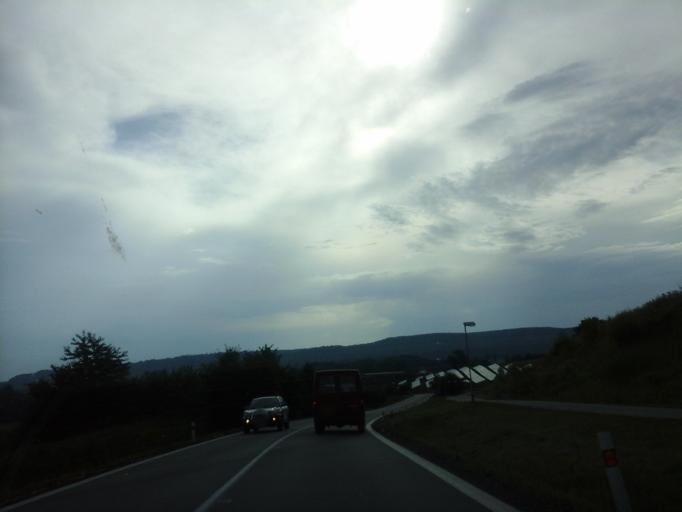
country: CZ
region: Pardubicky
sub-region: Okres Usti nad Orlici
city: Lanskroun
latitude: 49.8983
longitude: 16.5873
